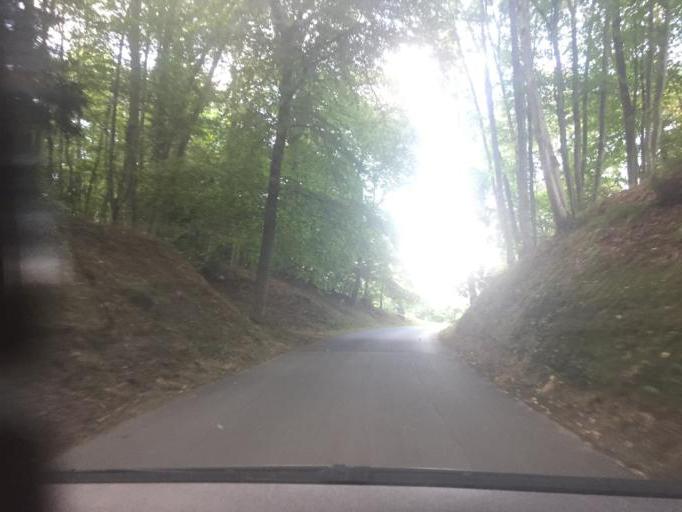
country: FR
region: Ile-de-France
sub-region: Departement des Yvelines
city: Jouy-en-Josas
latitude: 48.7618
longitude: 2.1590
